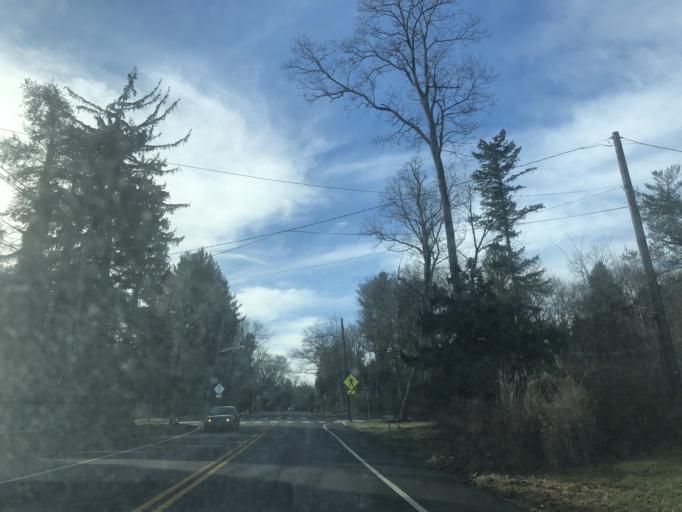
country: US
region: New Jersey
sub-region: Somerset County
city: Kingston
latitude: 40.3656
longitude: -74.6275
